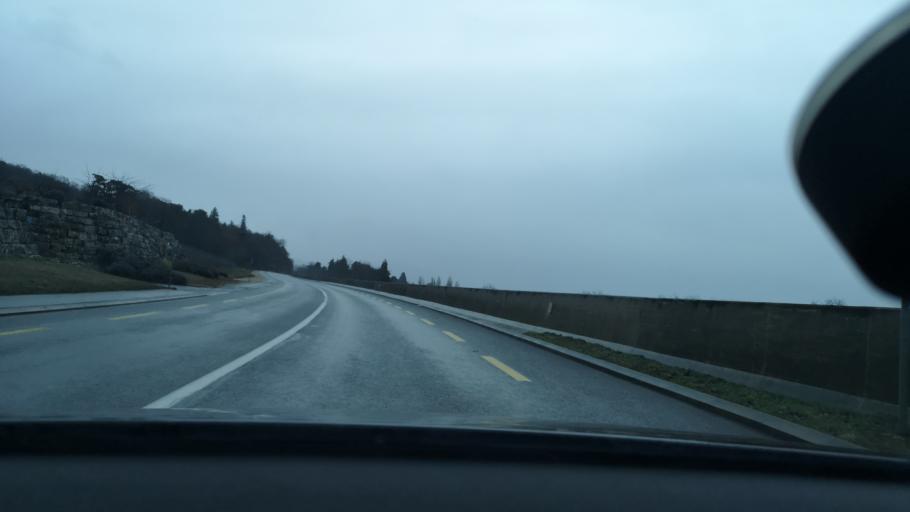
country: CH
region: Neuchatel
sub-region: Boudry District
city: Bevaix
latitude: 46.9129
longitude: 6.8010
